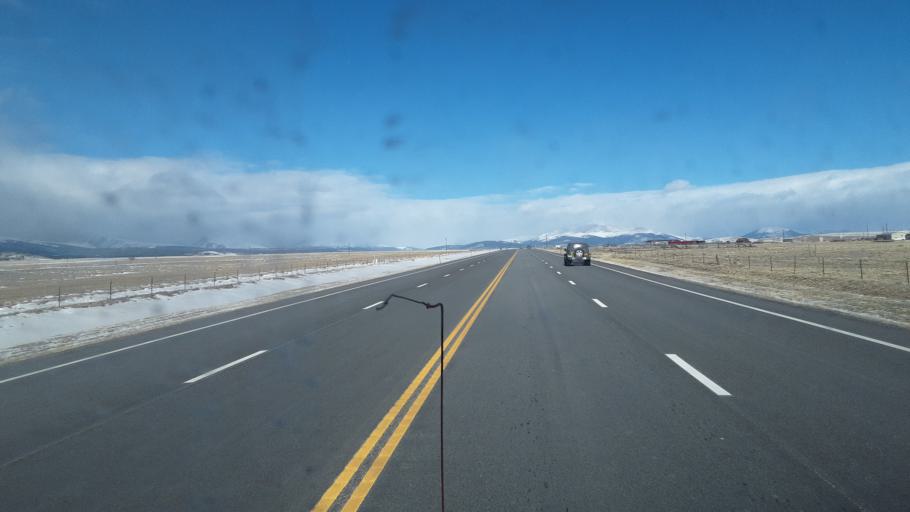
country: US
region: Colorado
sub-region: Park County
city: Fairplay
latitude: 39.1172
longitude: -105.9926
